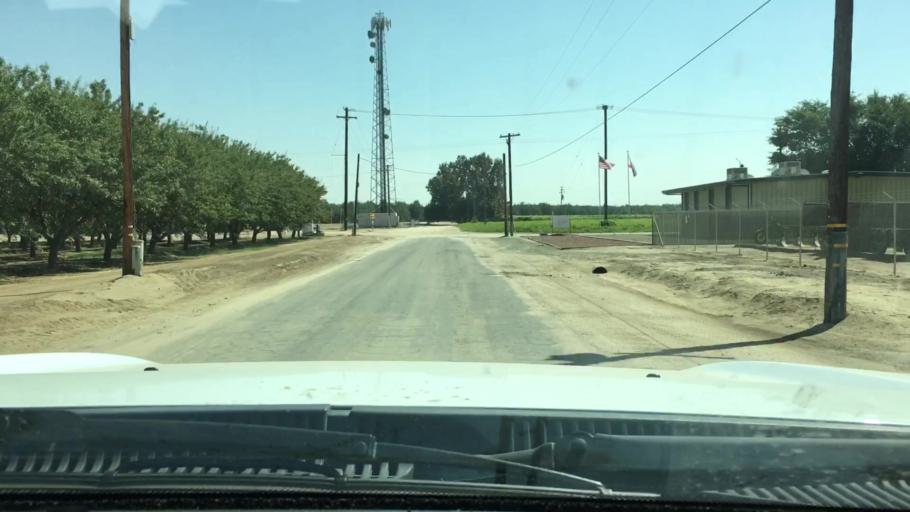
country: US
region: California
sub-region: Kern County
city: Shafter
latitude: 35.5364
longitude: -119.2699
